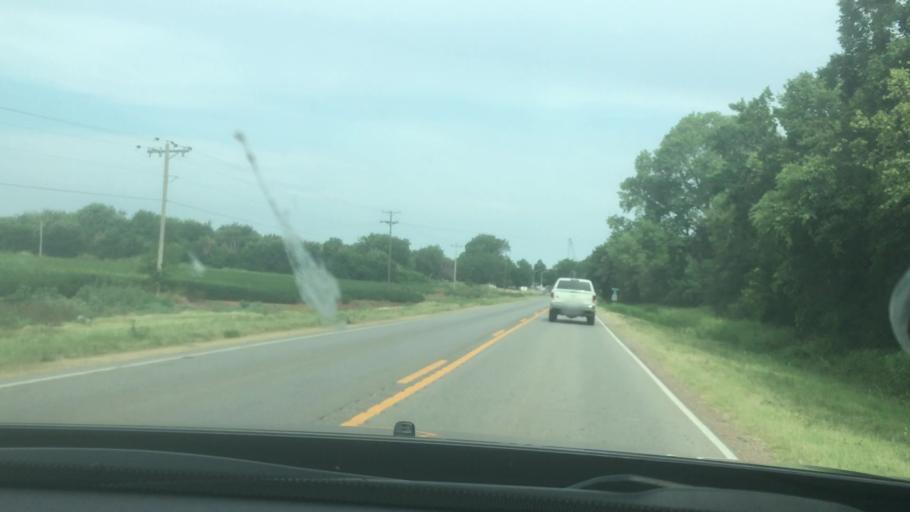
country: US
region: Oklahoma
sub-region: Garvin County
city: Maysville
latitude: 34.8163
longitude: -97.3977
